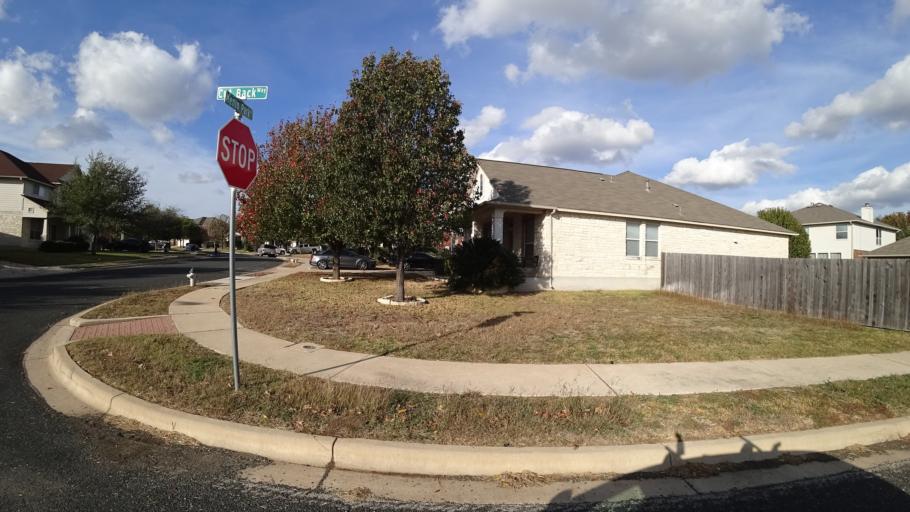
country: US
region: Texas
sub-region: Williamson County
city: Brushy Creek
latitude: 30.5054
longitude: -97.7252
